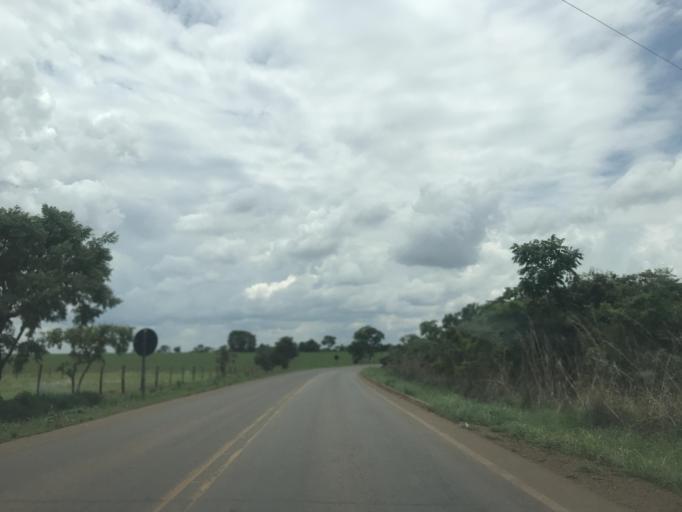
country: BR
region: Goias
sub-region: Vianopolis
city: Vianopolis
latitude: -16.7454
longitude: -48.4564
